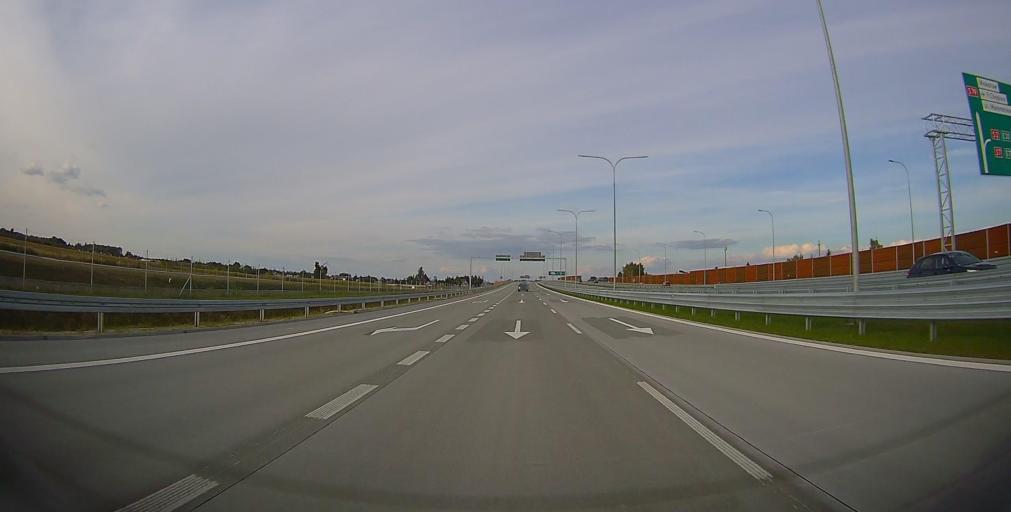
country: PL
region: Masovian Voivodeship
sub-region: Powiat piaseczynski
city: Mysiadlo
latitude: 52.1262
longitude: 20.9871
